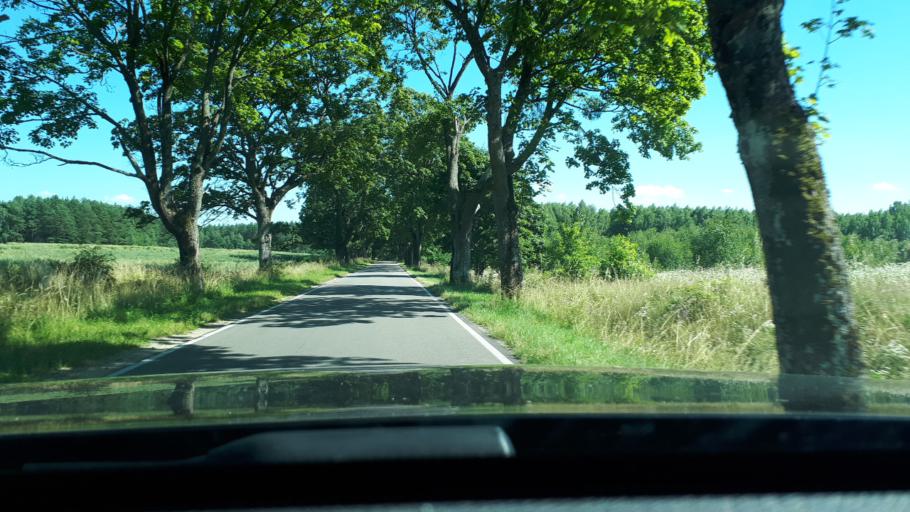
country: PL
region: Warmian-Masurian Voivodeship
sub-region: Powiat olsztynski
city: Stawiguda
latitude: 53.5943
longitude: 20.4283
